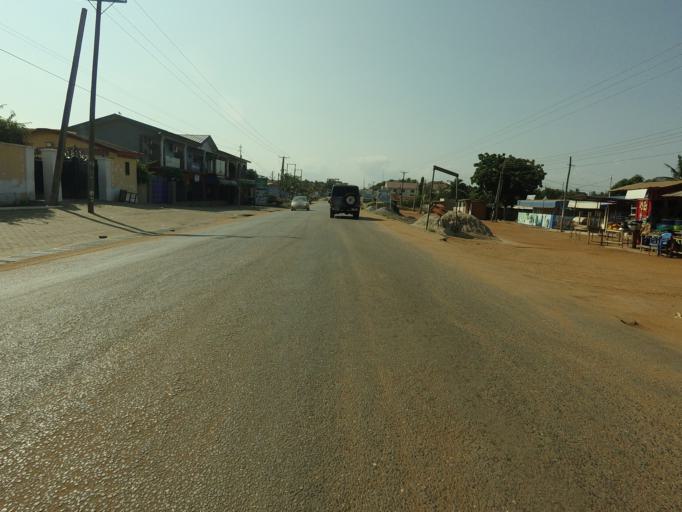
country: GH
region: Greater Accra
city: Teshi Old Town
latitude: 5.6004
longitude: -0.1034
